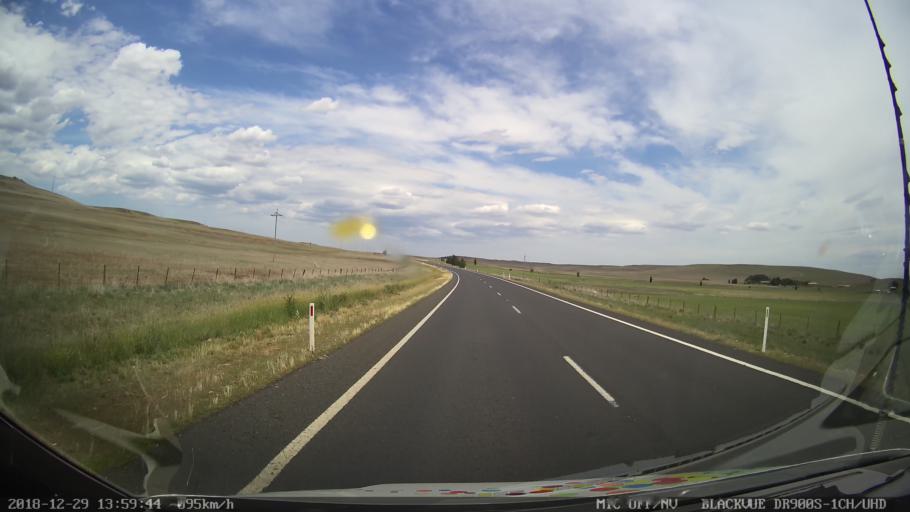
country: AU
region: New South Wales
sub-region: Cooma-Monaro
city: Cooma
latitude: -36.2567
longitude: 149.1508
